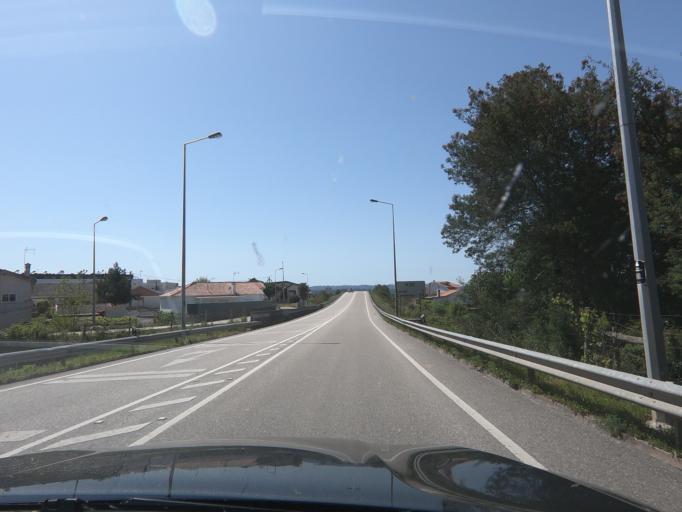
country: PT
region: Coimbra
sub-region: Lousa
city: Lousa
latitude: 40.1261
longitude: -8.2364
